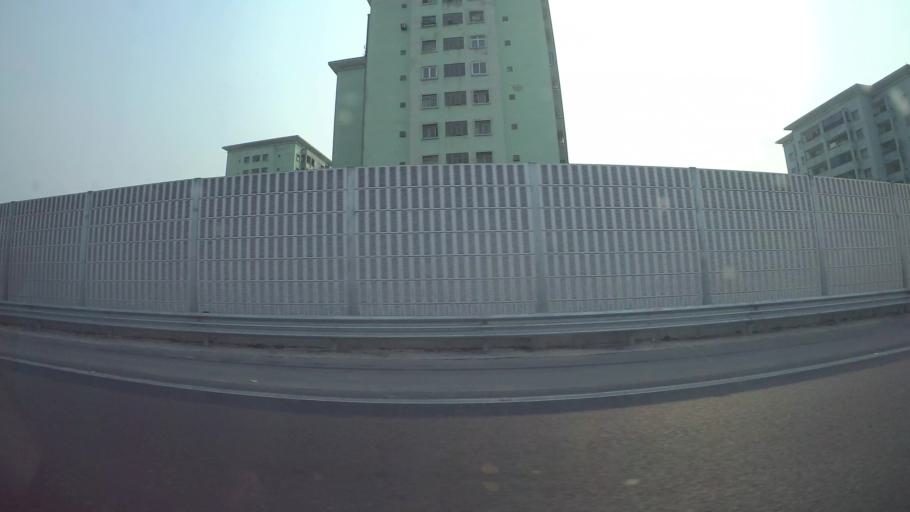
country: VN
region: Ha Noi
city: Van Dien
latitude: 20.9549
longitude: 105.8512
